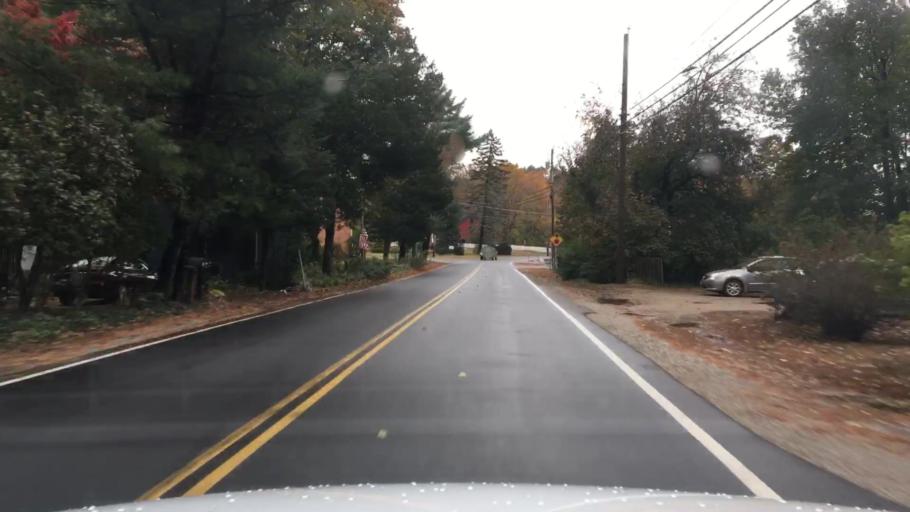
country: US
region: New Hampshire
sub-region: Strafford County
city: Lee
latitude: 43.1227
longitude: -71.0138
